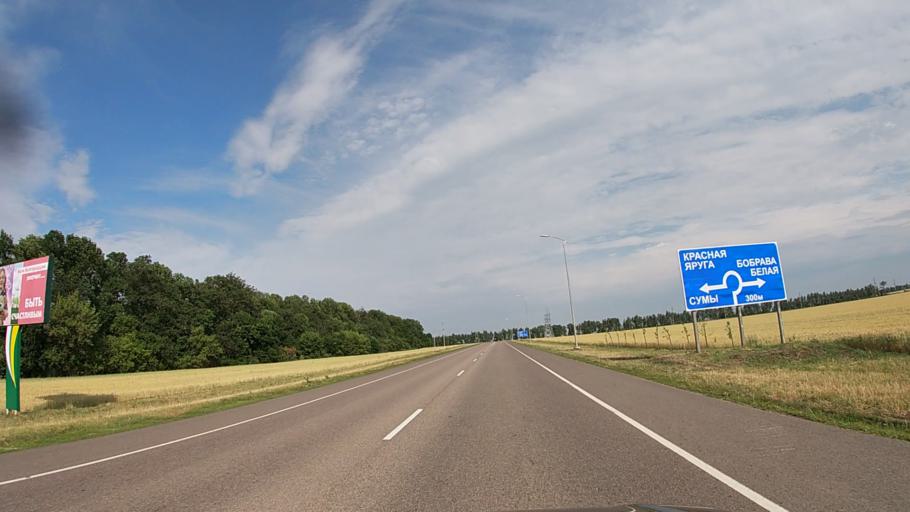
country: RU
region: Belgorod
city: Proletarskiy
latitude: 50.8291
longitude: 35.7722
